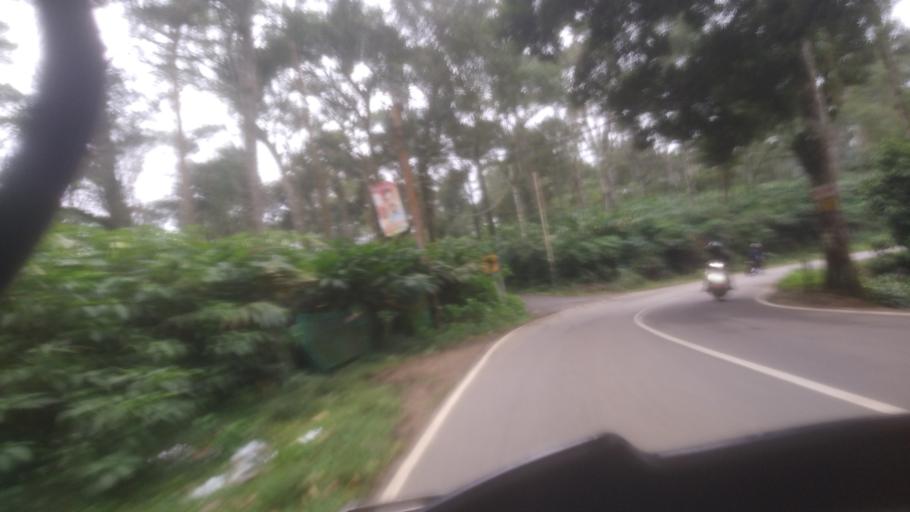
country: IN
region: Tamil Nadu
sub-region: Theni
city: Kombai
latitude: 9.8955
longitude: 77.1956
